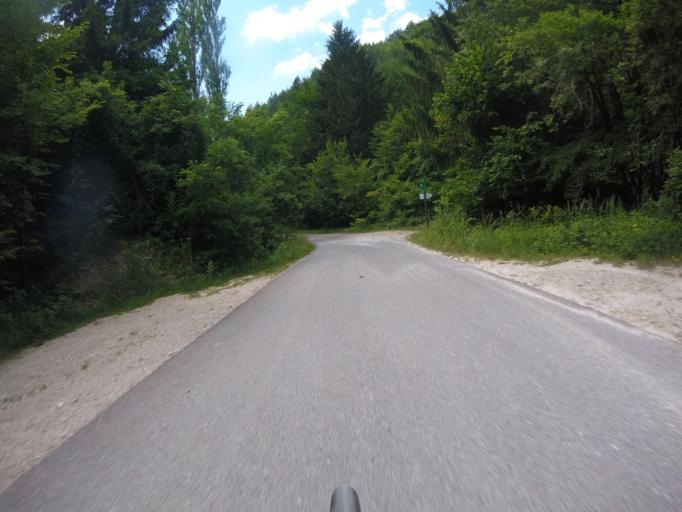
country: SI
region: Kostanjevica na Krki
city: Kostanjevica na Krki
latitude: 45.7639
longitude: 15.3982
